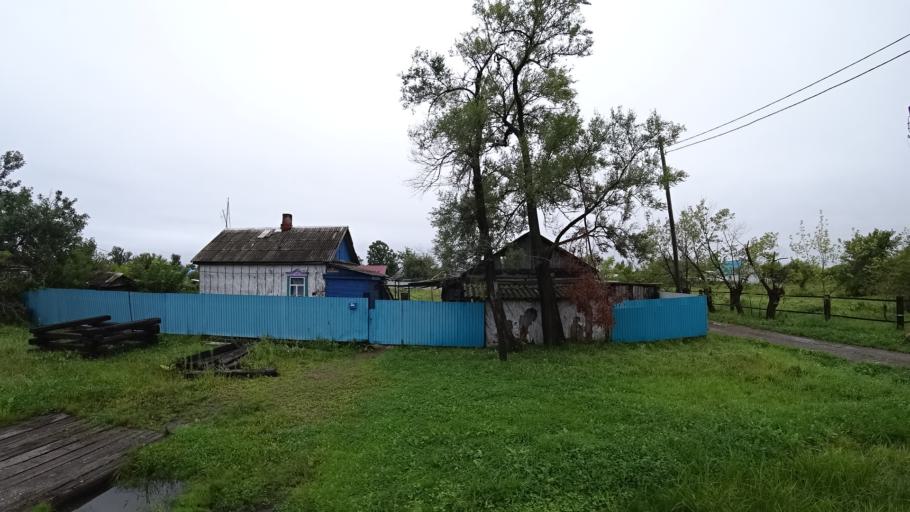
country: RU
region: Primorskiy
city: Monastyrishche
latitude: 44.2119
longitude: 132.4310
